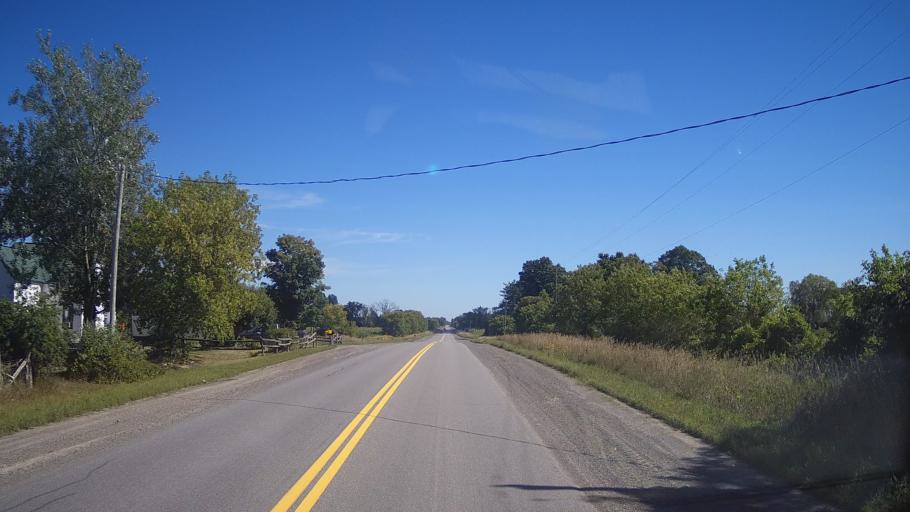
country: CA
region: Ontario
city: Bells Corners
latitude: 45.0384
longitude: -75.7085
